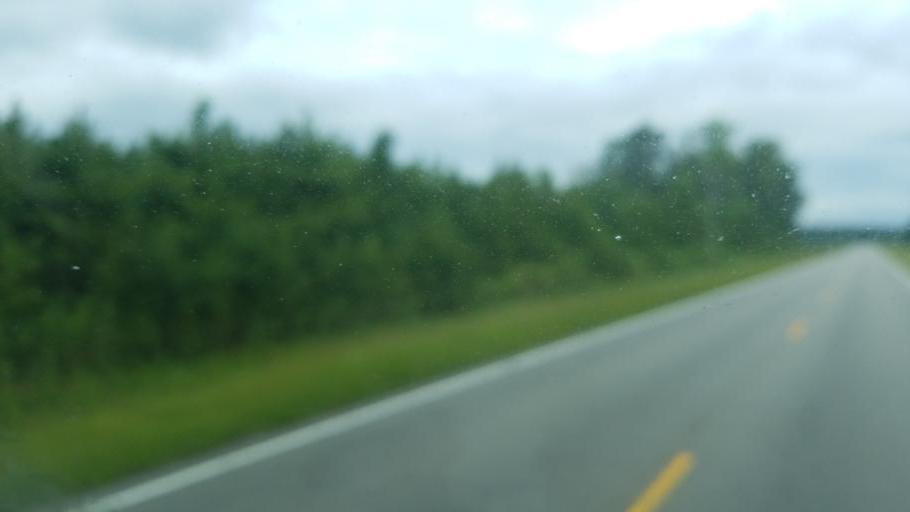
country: US
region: North Carolina
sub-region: Tyrrell County
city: Columbia
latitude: 35.9314
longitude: -76.1787
